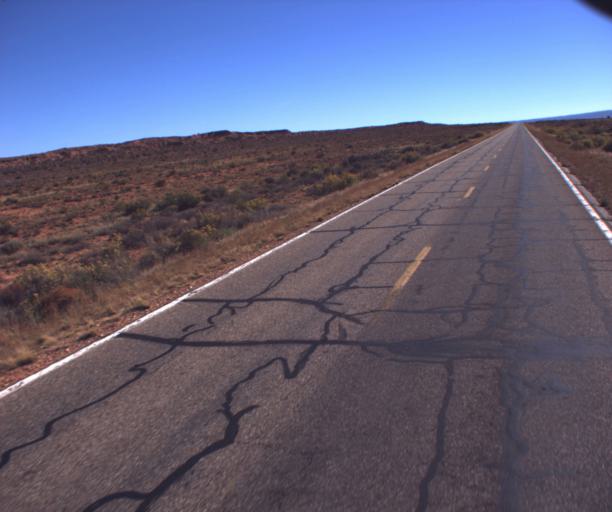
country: US
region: Arizona
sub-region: Coconino County
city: Fredonia
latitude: 36.9334
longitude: -112.5018
